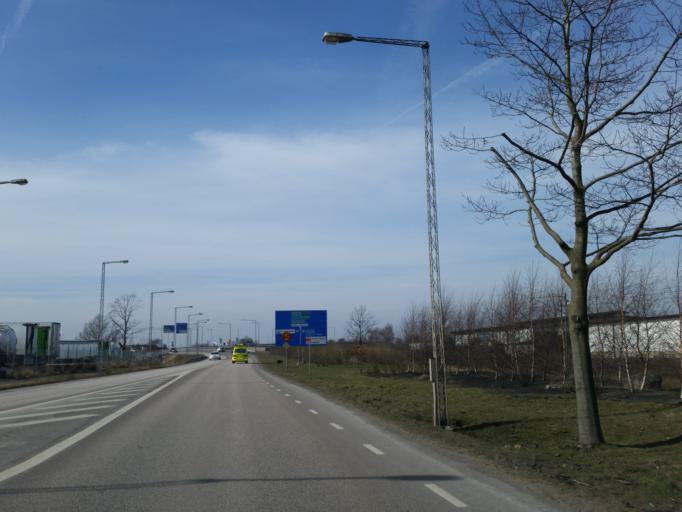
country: SE
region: Kalmar
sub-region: Kalmar Kommun
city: Rinkabyholm
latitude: 56.6712
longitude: 16.3105
